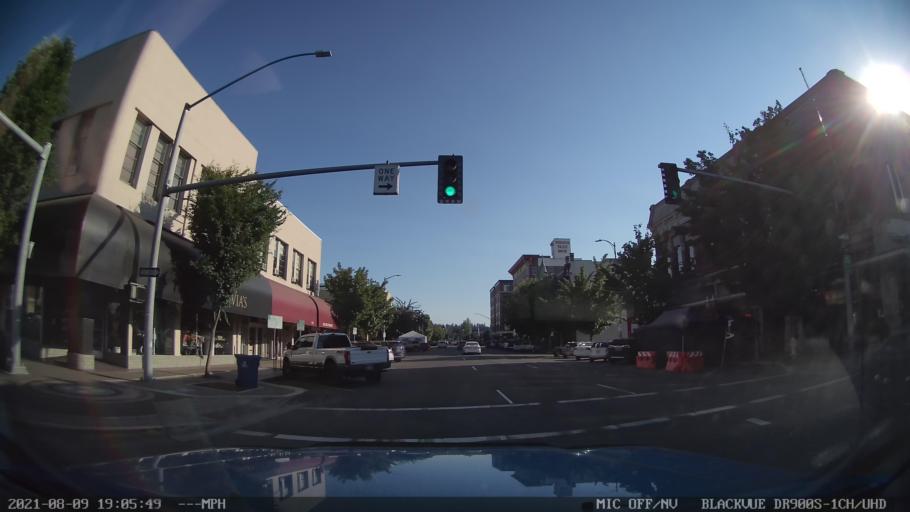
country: US
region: Oregon
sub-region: Marion County
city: Salem
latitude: 44.9418
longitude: -123.0401
